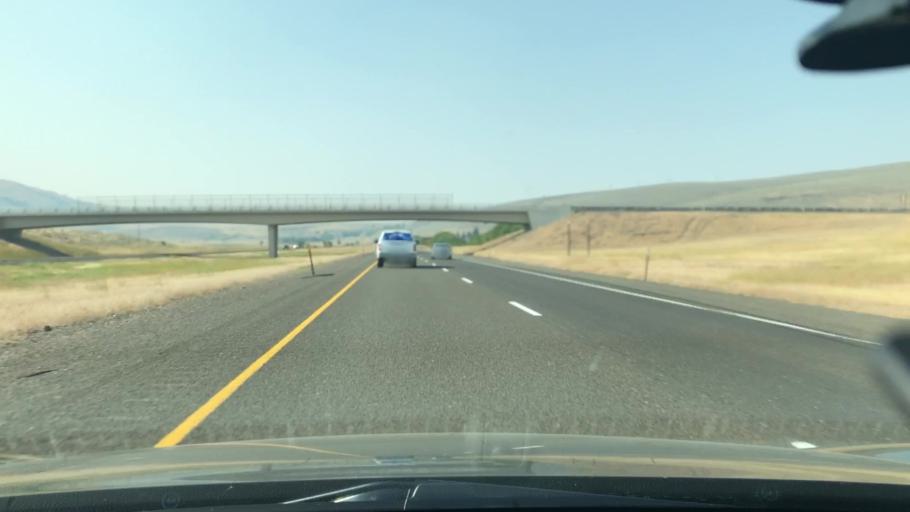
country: US
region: Oregon
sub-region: Union County
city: Union
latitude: 45.1228
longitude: -117.9621
